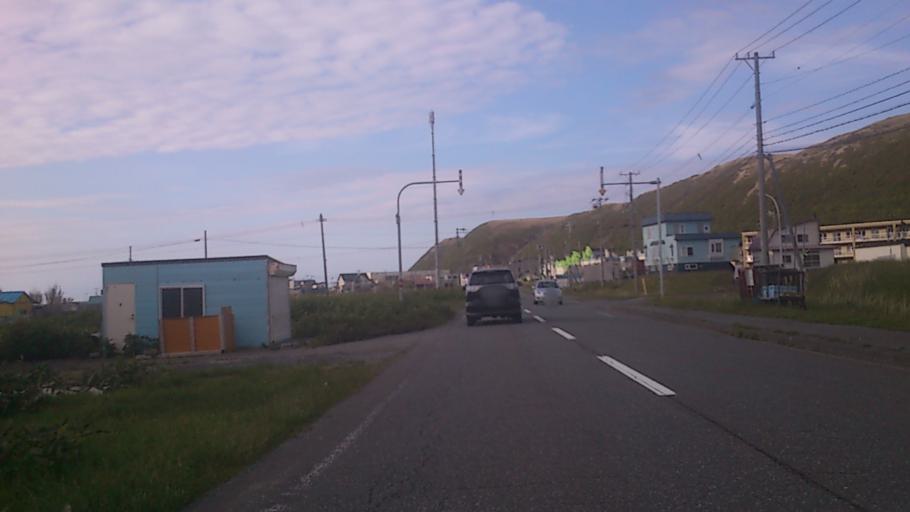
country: JP
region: Hokkaido
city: Wakkanai
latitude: 45.4141
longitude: 141.6358
